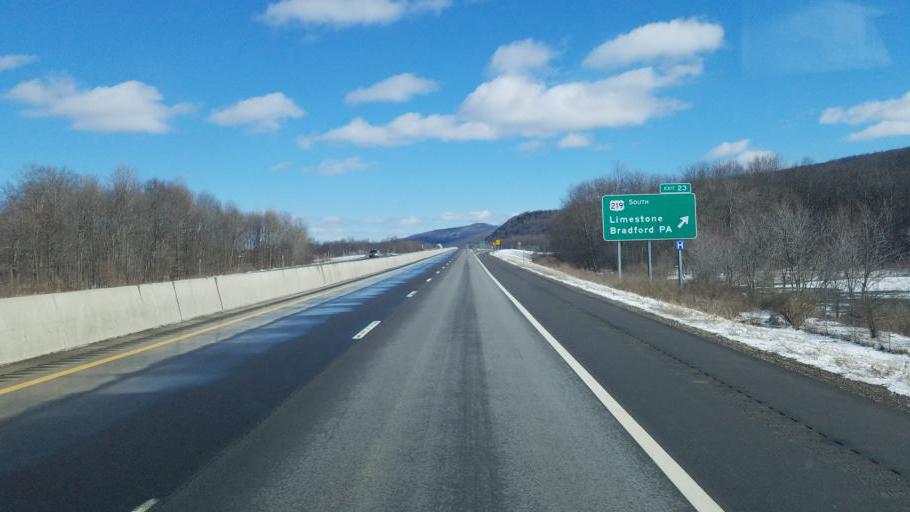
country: US
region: New York
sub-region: Cattaraugus County
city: Salamanca
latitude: 42.0894
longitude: -78.6373
